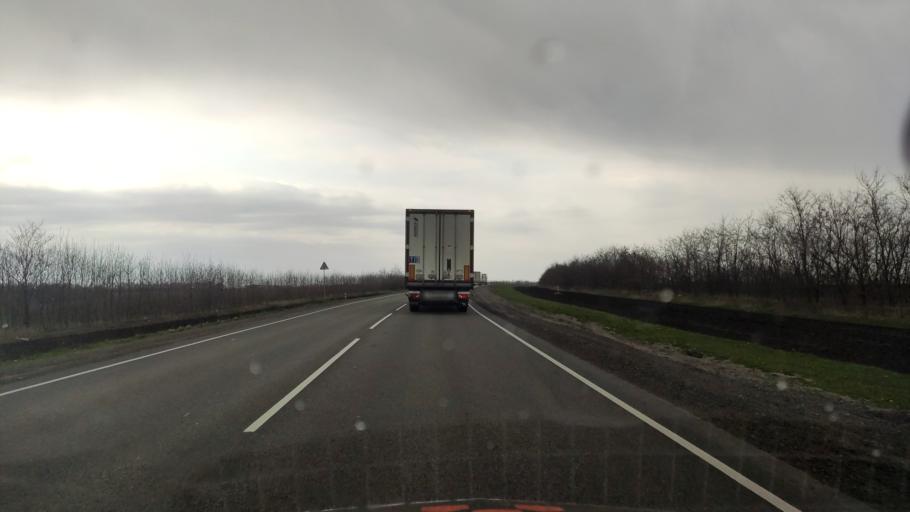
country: RU
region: Voronezj
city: Nizhnedevitsk
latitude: 51.5660
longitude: 38.3464
